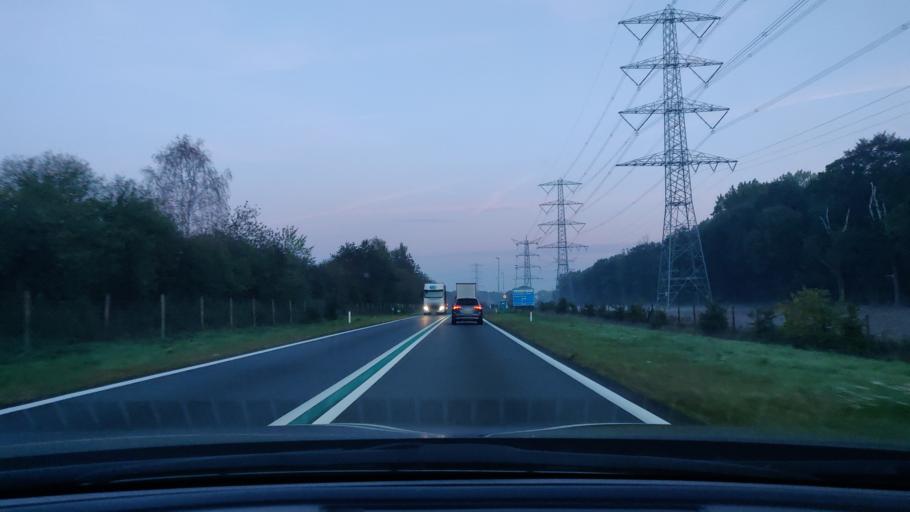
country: NL
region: Overijssel
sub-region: Gemeente Enschede
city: Enschede
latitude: 52.1991
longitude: 6.9357
